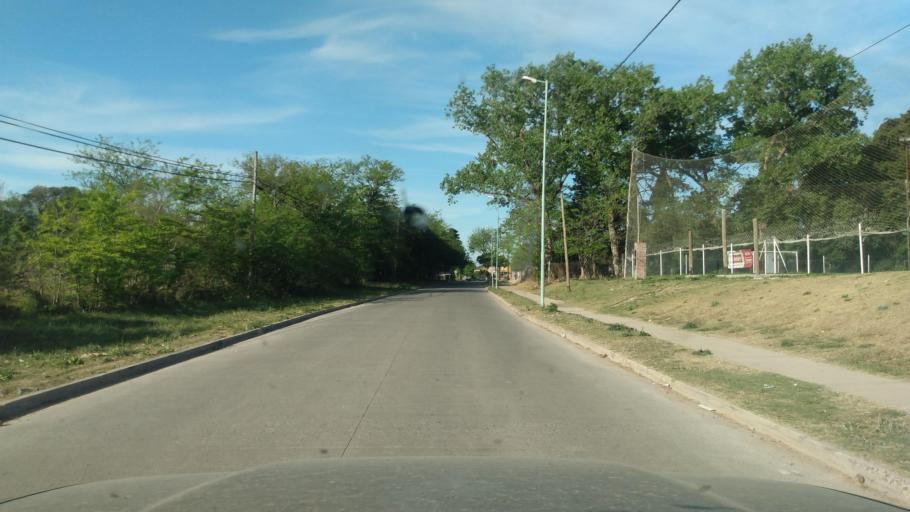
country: AR
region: Buenos Aires
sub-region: Partido de Lujan
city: Lujan
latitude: -34.5821
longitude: -59.1241
